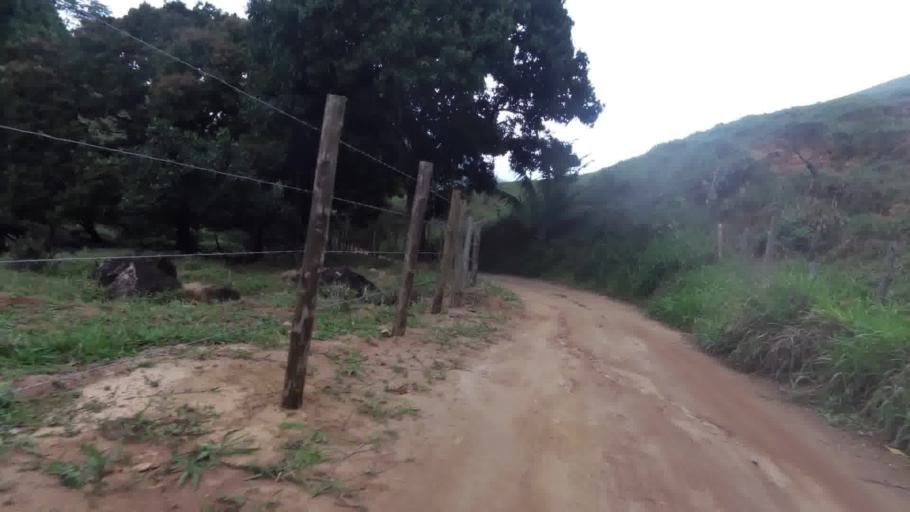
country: BR
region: Espirito Santo
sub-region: Alfredo Chaves
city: Alfredo Chaves
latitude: -20.6277
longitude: -40.7528
